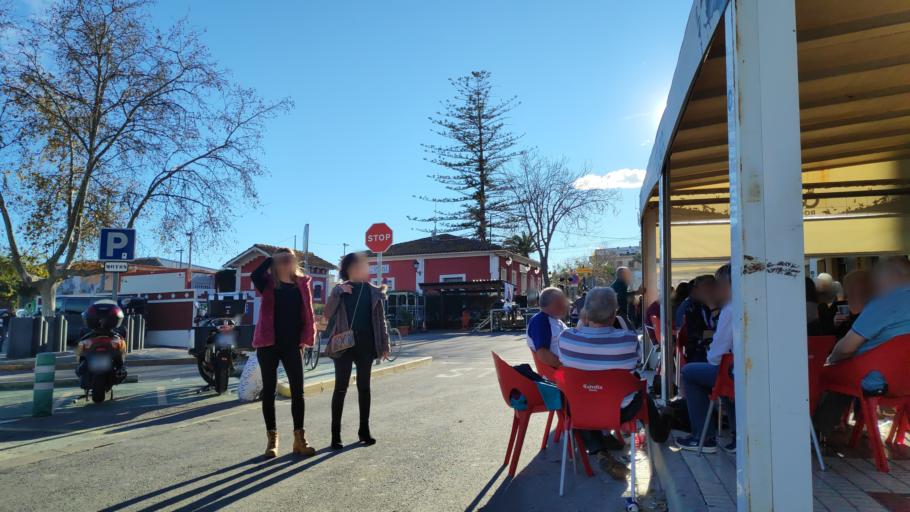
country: ES
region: Valencia
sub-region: Provincia de Castello
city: Benicassim
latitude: 40.0542
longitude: 0.0646
